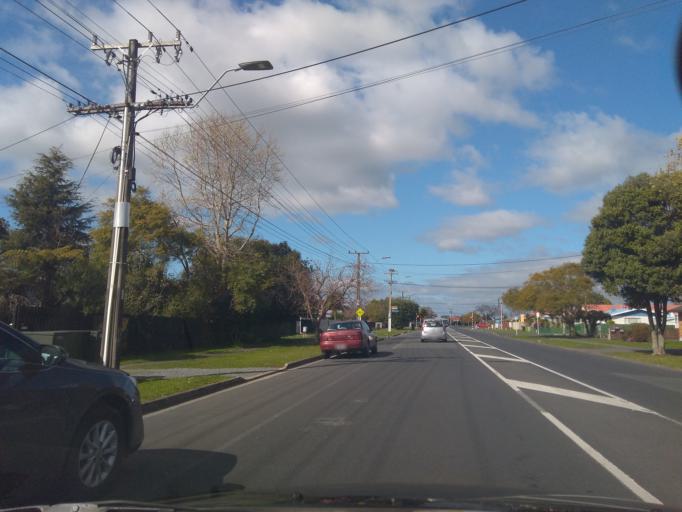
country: NZ
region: Northland
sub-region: Whangarei
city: Whangarei
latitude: -35.6896
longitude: 174.3271
